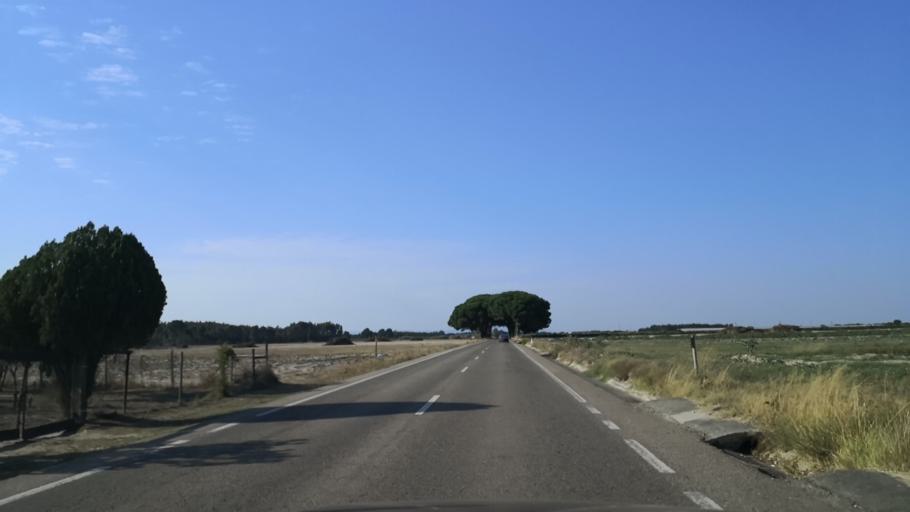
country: PT
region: Santarem
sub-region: Almeirim
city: Almeirim
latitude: 39.1586
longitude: -8.6204
